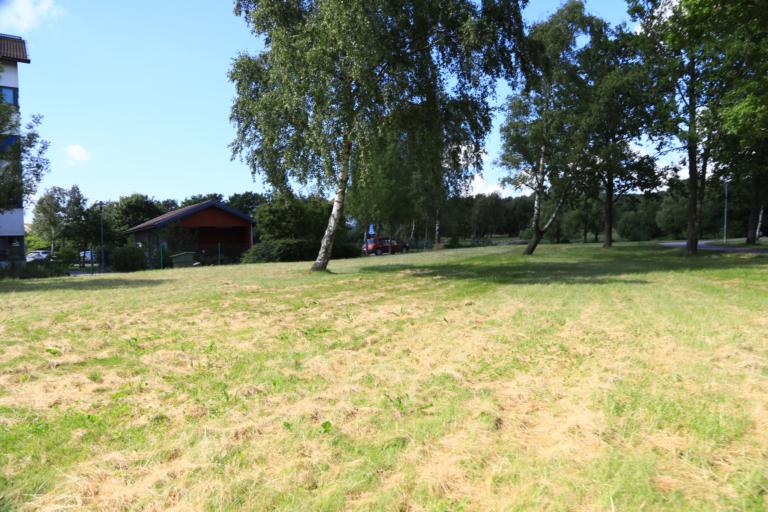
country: SE
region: Halland
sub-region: Varbergs Kommun
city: Traslovslage
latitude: 57.0881
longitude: 12.2746
